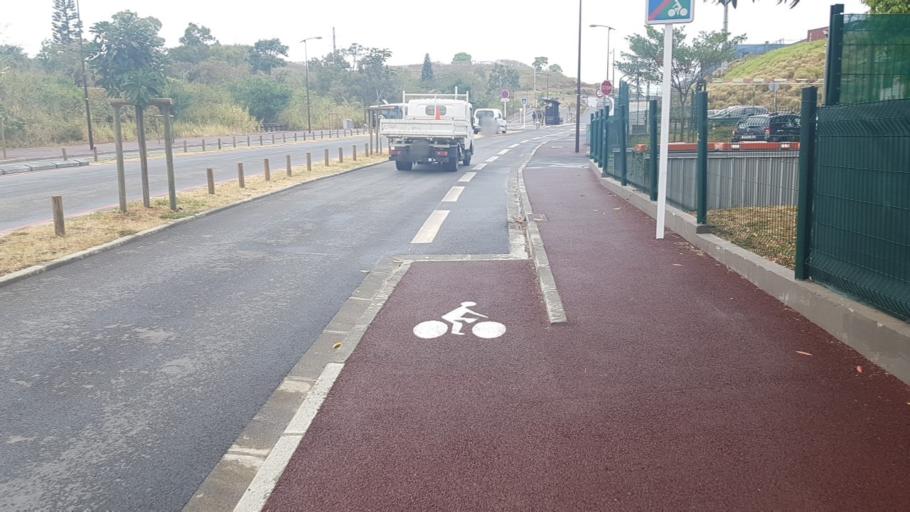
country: NC
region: South Province
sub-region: Noumea
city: Noumea
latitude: -22.2211
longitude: 166.4756
